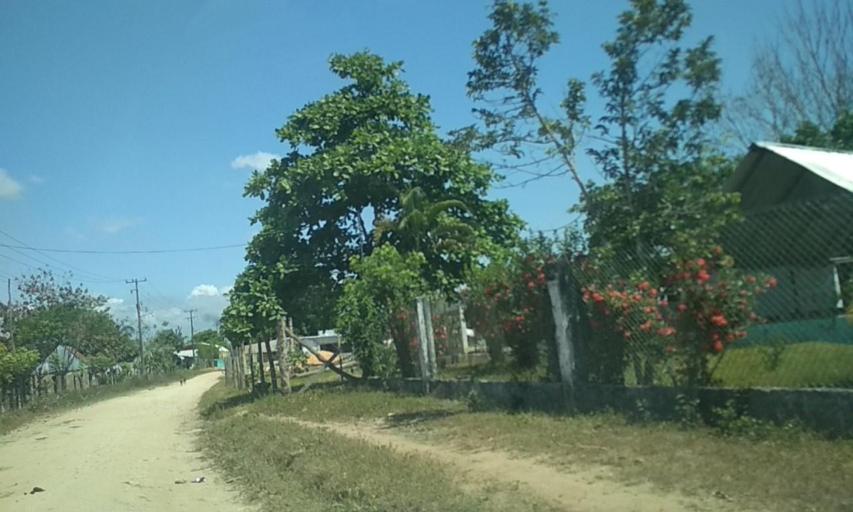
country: MX
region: Veracruz
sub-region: Moloacan
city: Cuichapa
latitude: 17.7861
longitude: -94.1946
